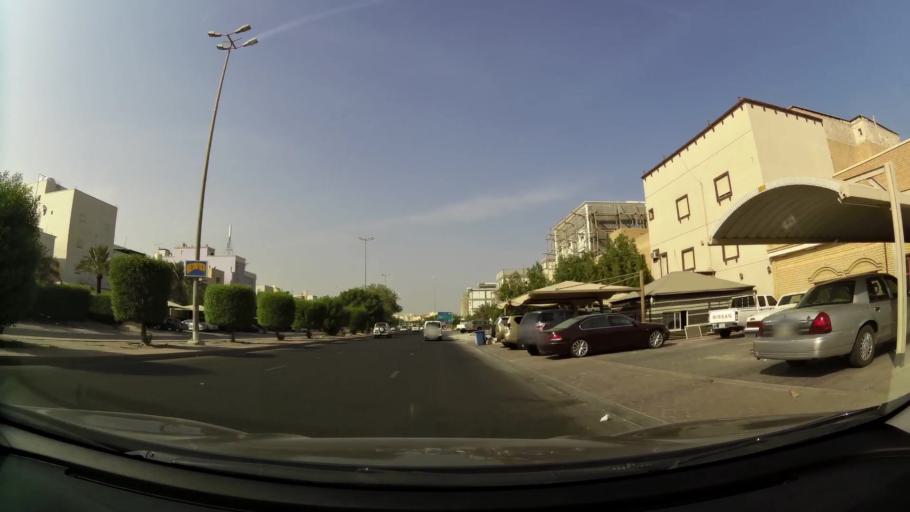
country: KW
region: Mubarak al Kabir
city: Mubarak al Kabir
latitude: 29.1765
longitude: 48.0841
